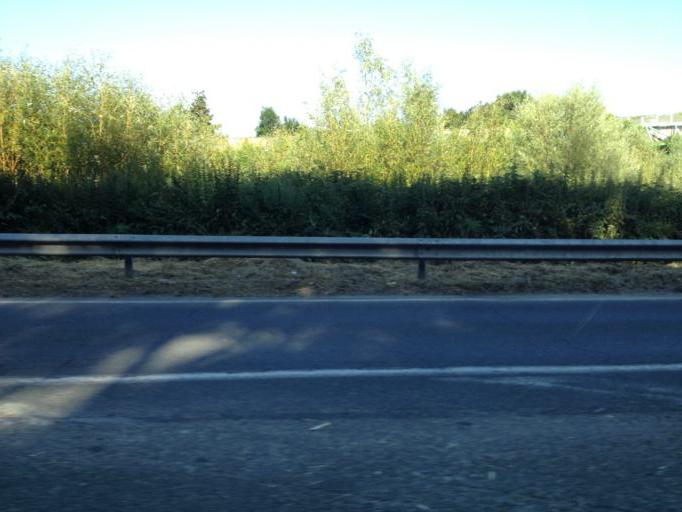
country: FR
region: Ile-de-France
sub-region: Departement de l'Essonne
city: Orsay
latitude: 48.7011
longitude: 2.1916
